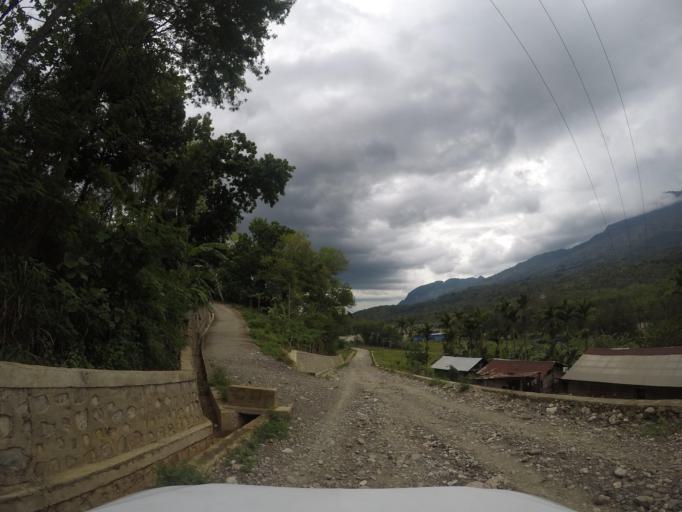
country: TL
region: Bobonaro
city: Maliana
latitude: -8.9761
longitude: 125.2211
